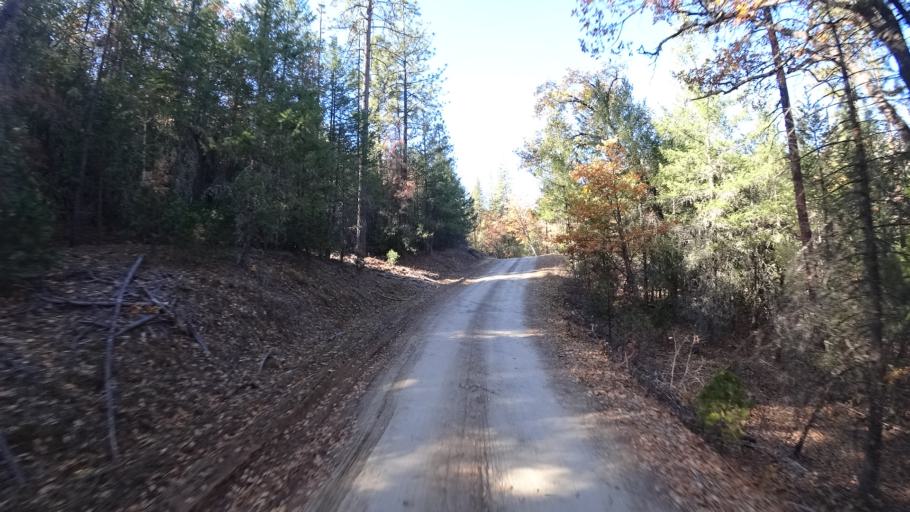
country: US
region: California
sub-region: Siskiyou County
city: Yreka
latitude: 41.8604
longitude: -122.8215
